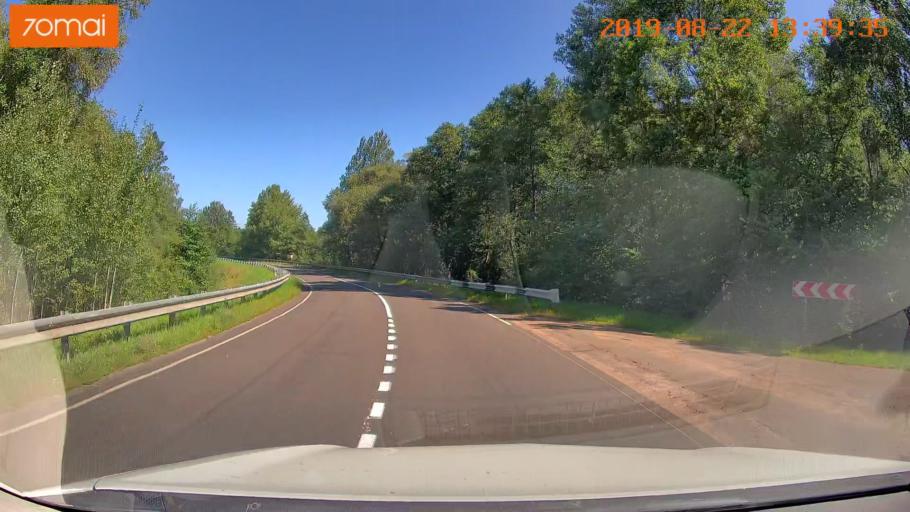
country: BY
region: Minsk
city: Staryya Darohi
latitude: 53.2273
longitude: 28.3526
